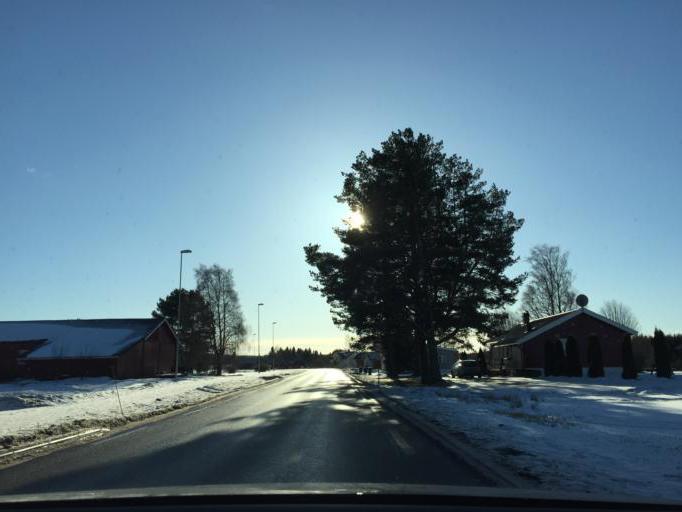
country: NO
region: Akershus
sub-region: Nes
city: Fjellfoten
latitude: 60.1054
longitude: 11.4792
